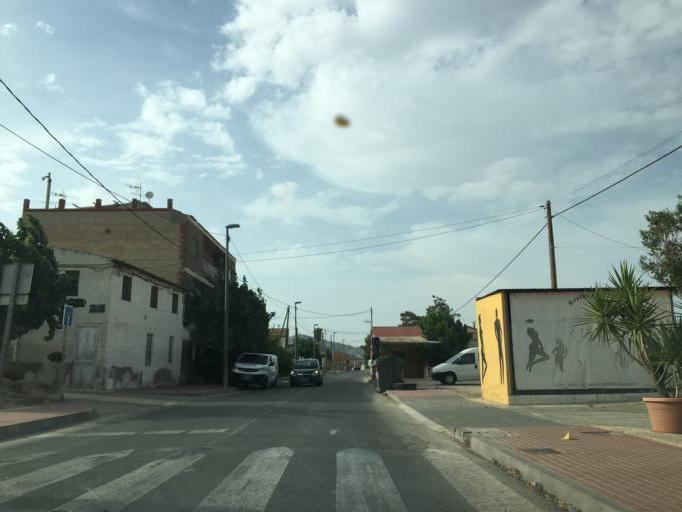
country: ES
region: Murcia
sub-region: Murcia
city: Murcia
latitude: 38.0097
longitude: -1.0806
